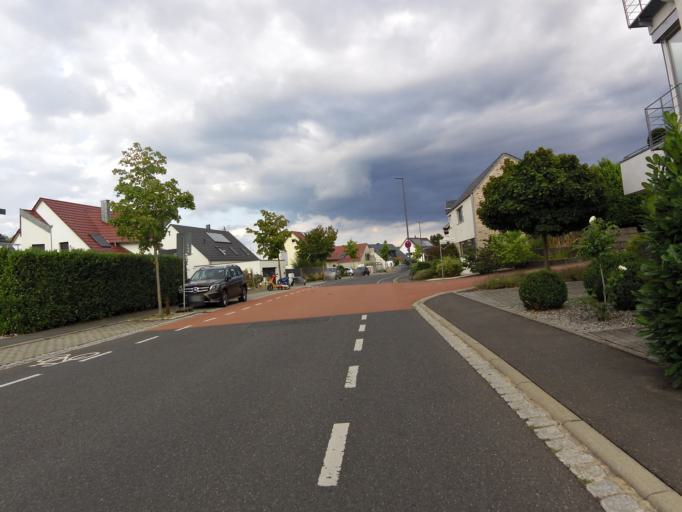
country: DE
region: Bavaria
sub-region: Regierungsbezirk Unterfranken
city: Hochberg
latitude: 49.7804
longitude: 9.8686
